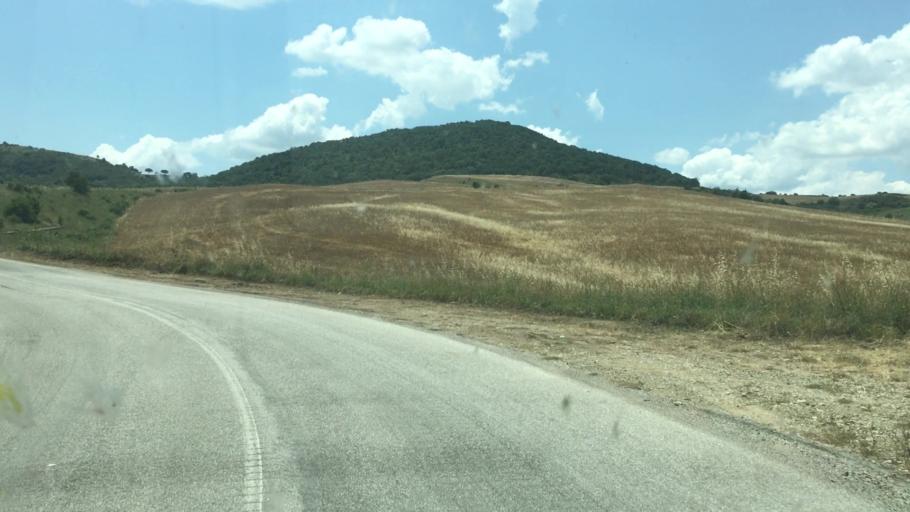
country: IT
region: Basilicate
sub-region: Provincia di Potenza
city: Tolve
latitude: 40.6922
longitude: 15.9870
